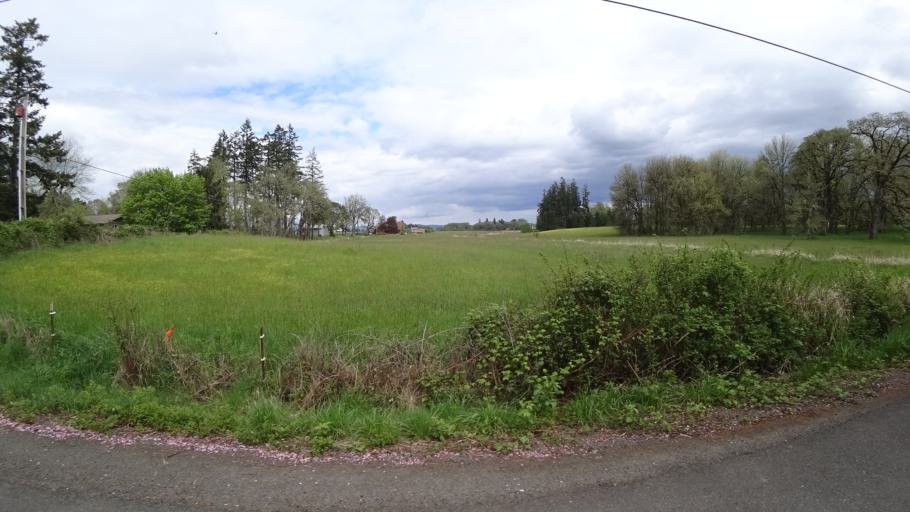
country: US
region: Oregon
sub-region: Washington County
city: Hillsboro
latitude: 45.5616
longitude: -122.9528
